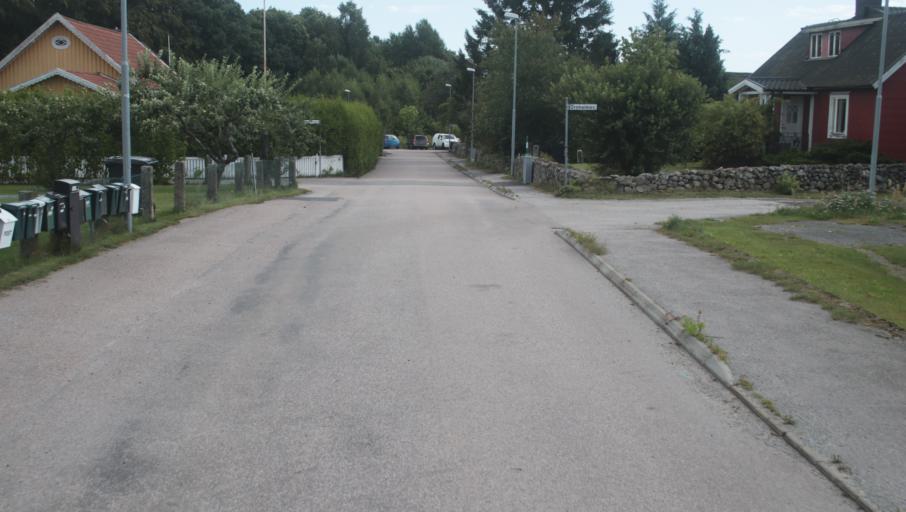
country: SE
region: Blekinge
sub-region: Karlshamns Kommun
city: Morrum
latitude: 56.1644
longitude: 14.6817
